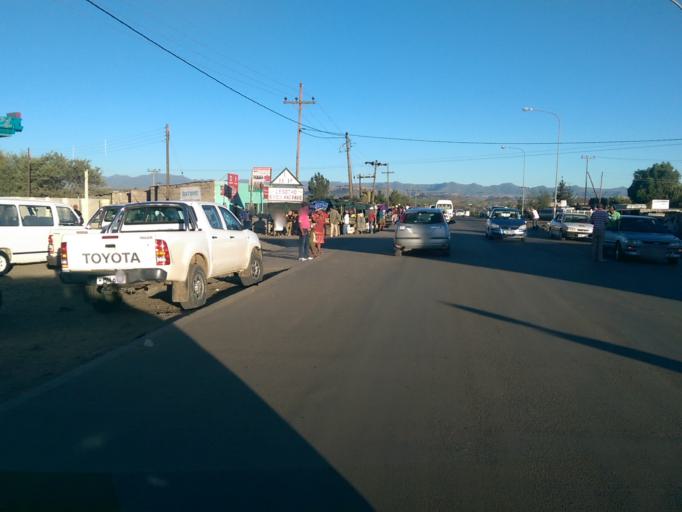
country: LS
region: Maseru
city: Maseru
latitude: -29.3689
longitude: 27.5375
